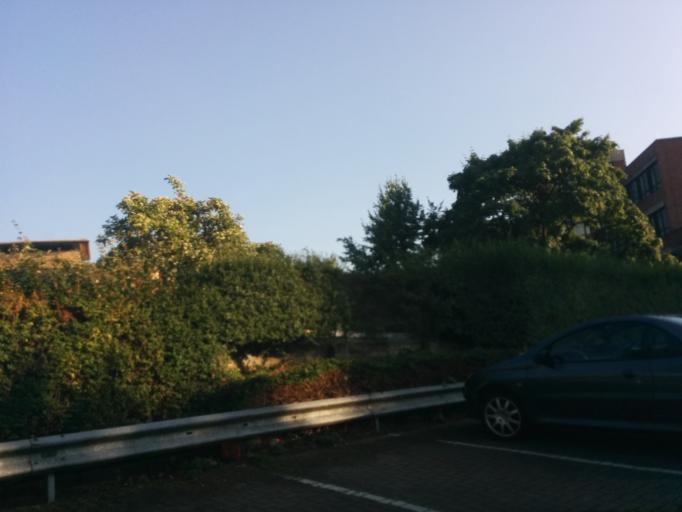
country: DE
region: North Rhine-Westphalia
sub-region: Regierungsbezirk Munster
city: Rheine
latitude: 52.2766
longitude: 7.4310
